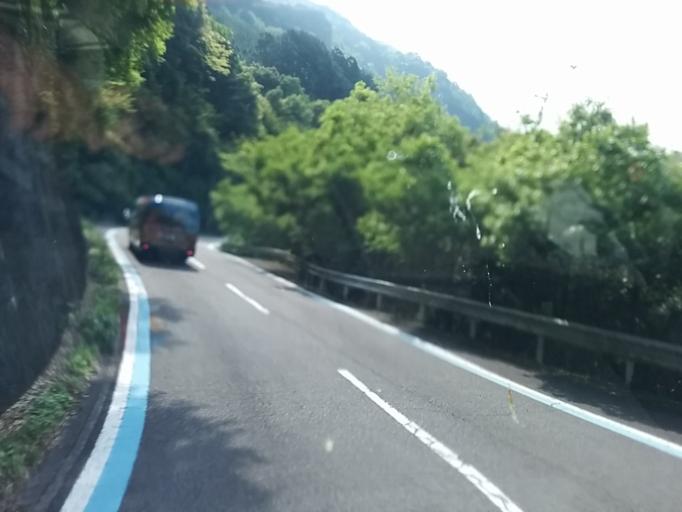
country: JP
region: Ehime
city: Niihama
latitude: 33.8979
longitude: 133.3084
